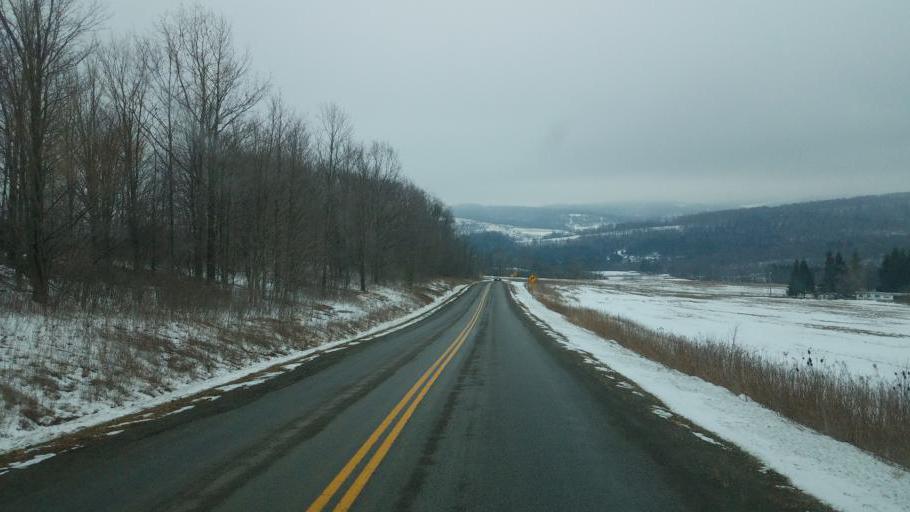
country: US
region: Pennsylvania
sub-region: Tioga County
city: Westfield
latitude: 42.0462
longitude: -77.5377
